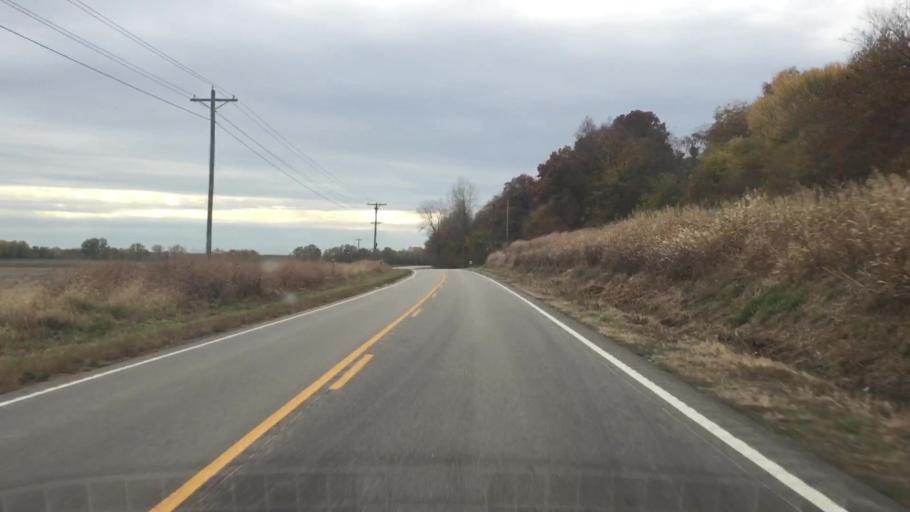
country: US
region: Missouri
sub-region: Callaway County
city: Holts Summit
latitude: 38.5840
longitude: -92.0521
